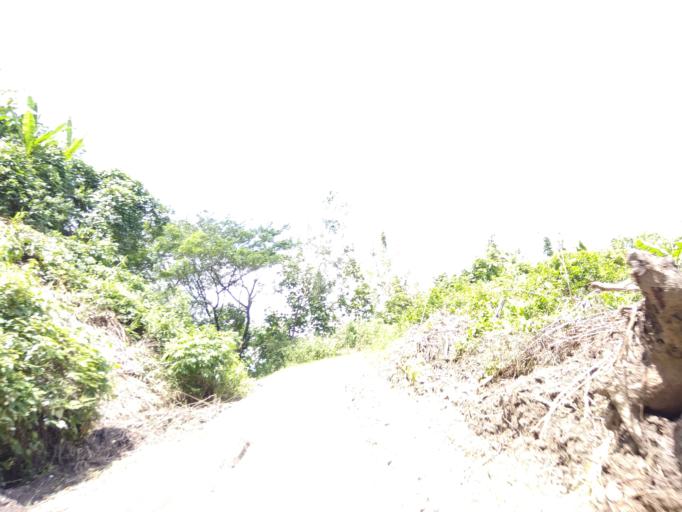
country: BD
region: Chittagong
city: Cox's Bazar
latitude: 21.6673
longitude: 92.3540
